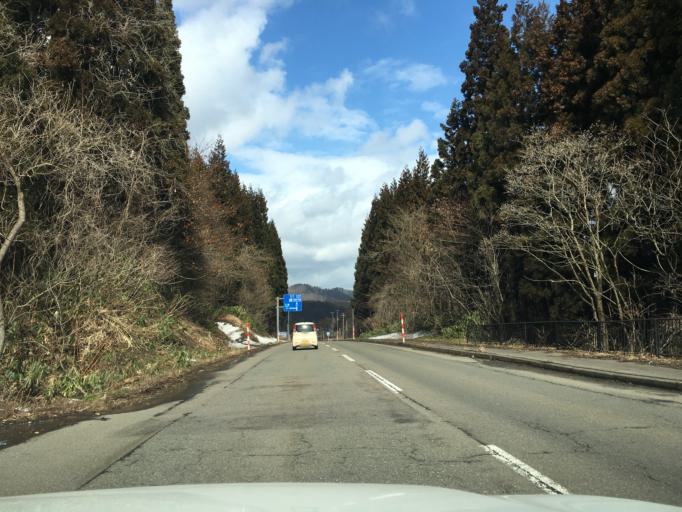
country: JP
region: Akita
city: Takanosu
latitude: 40.0213
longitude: 140.2748
